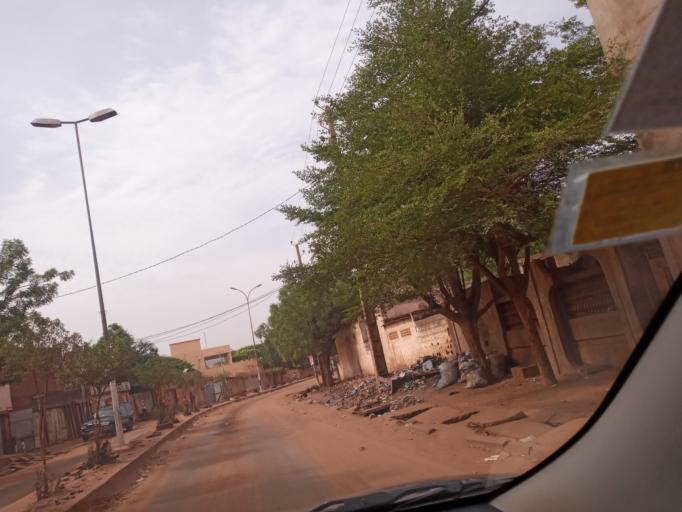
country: ML
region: Bamako
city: Bamako
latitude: 12.6774
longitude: -7.9244
